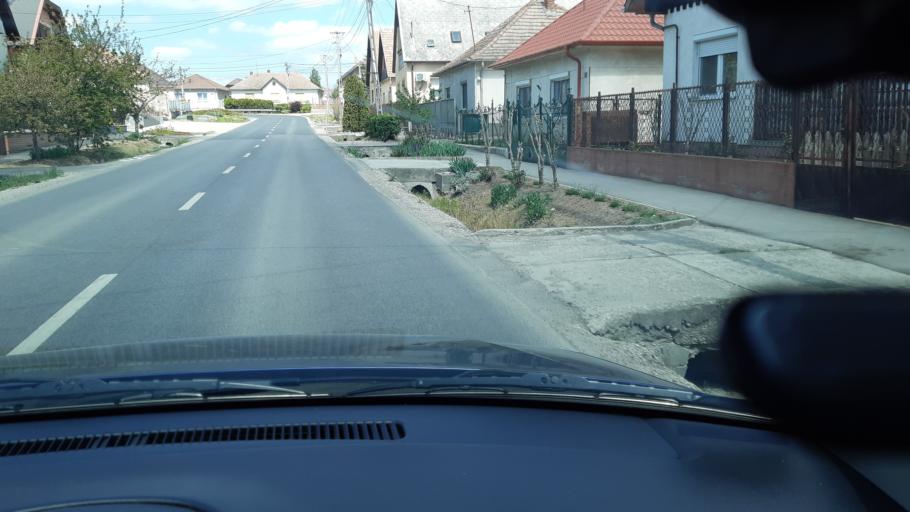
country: HU
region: Pest
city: Nagytarcsa
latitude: 47.5296
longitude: 19.2832
